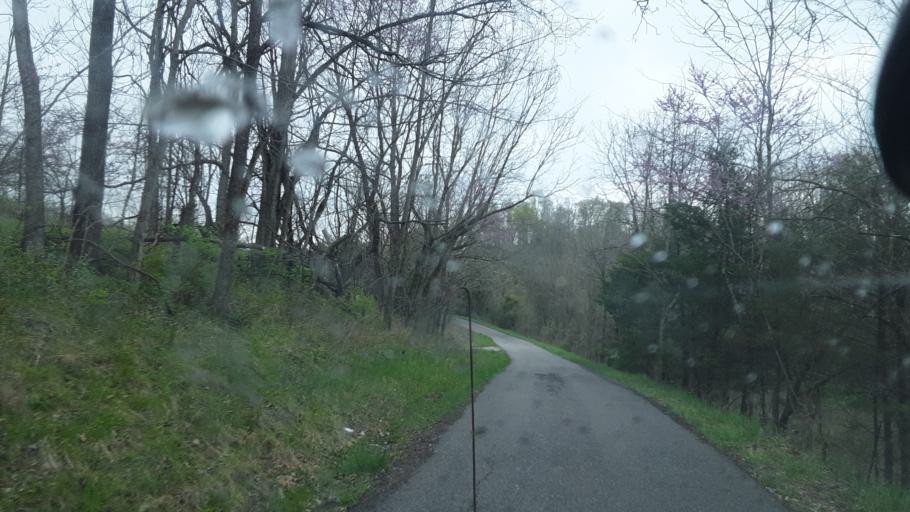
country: US
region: Kentucky
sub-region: Owen County
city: Owenton
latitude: 38.6454
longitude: -84.7876
